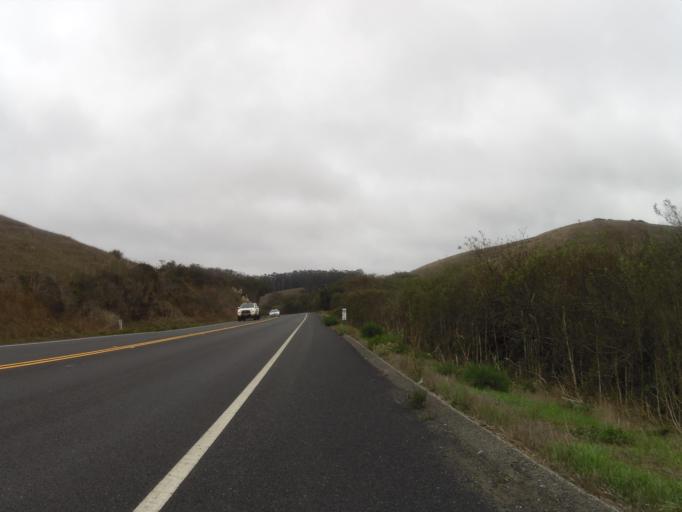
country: US
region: California
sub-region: Sonoma County
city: Bodega Bay
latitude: 38.3272
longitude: -123.0009
